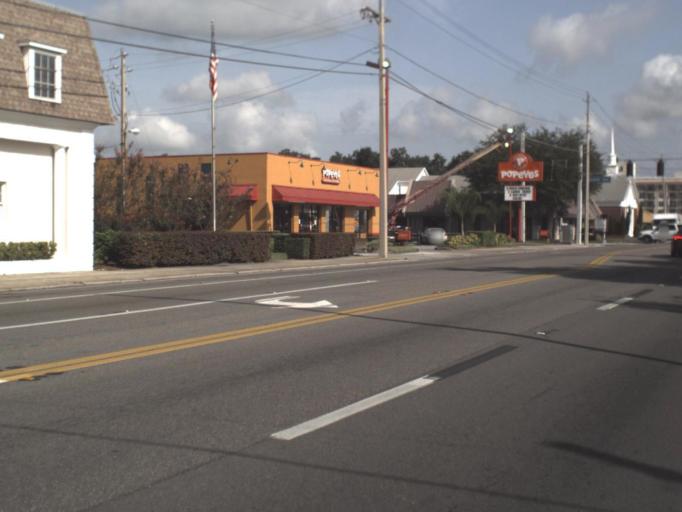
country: US
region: Florida
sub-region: Polk County
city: Winter Haven
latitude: 28.0215
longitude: -81.7330
